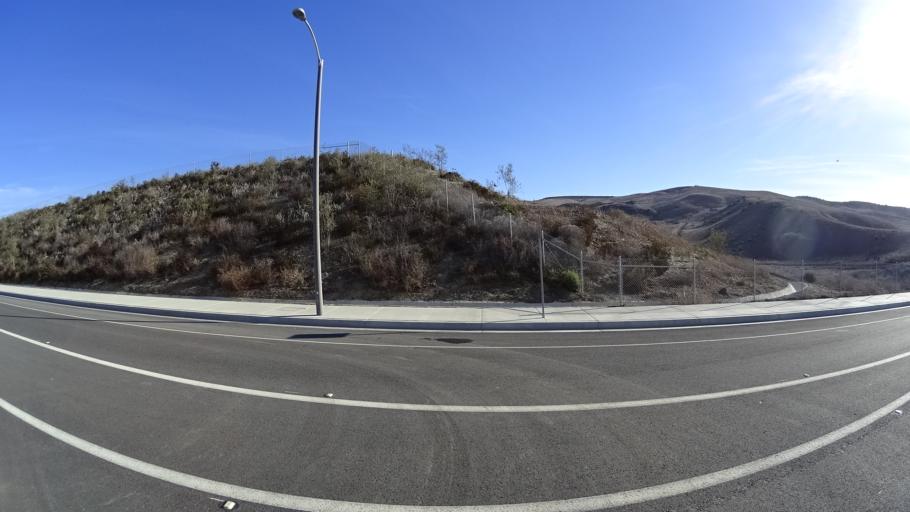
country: US
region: California
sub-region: Orange County
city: San Juan Capistrano
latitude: 33.4921
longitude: -117.6145
